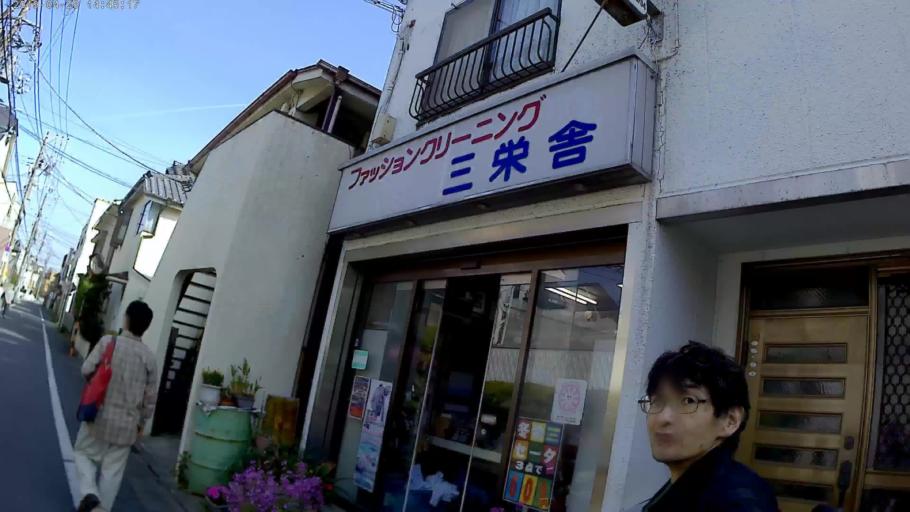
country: JP
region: Kanagawa
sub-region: Kawasaki-shi
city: Kawasaki
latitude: 35.5533
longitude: 139.7093
